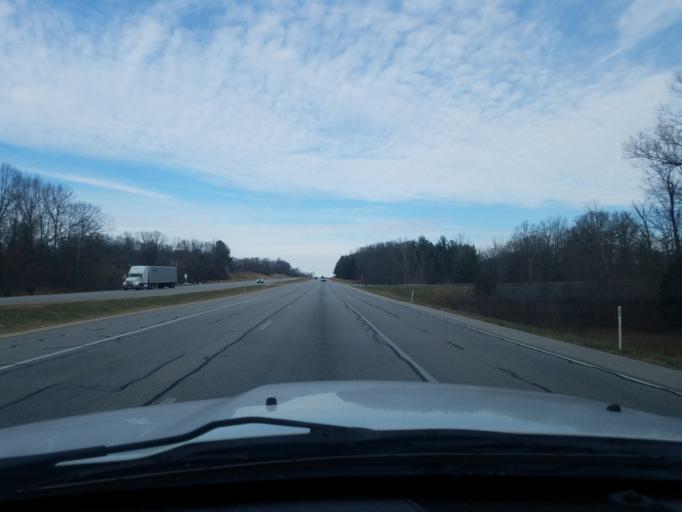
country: US
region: Indiana
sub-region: Lawrence County
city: Oolitic
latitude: 38.9546
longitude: -86.5521
